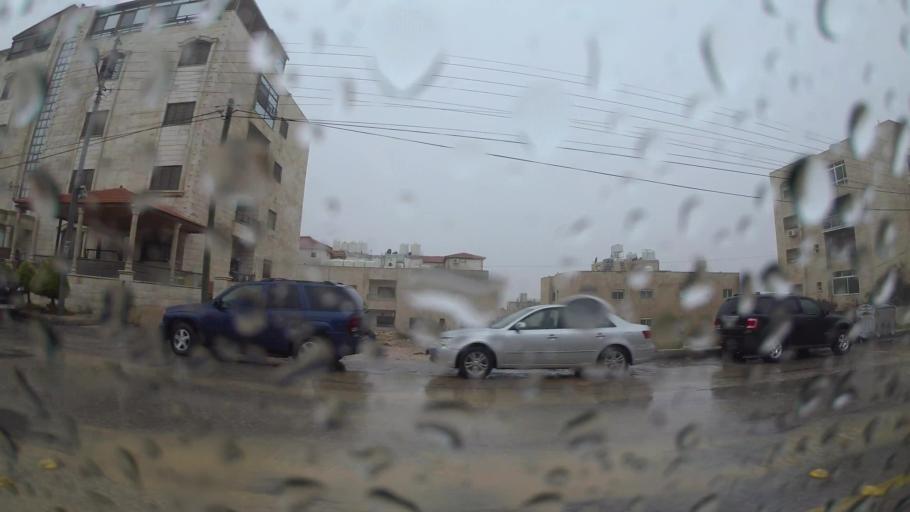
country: JO
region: Amman
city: Al Jubayhah
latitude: 32.0155
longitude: 35.8845
